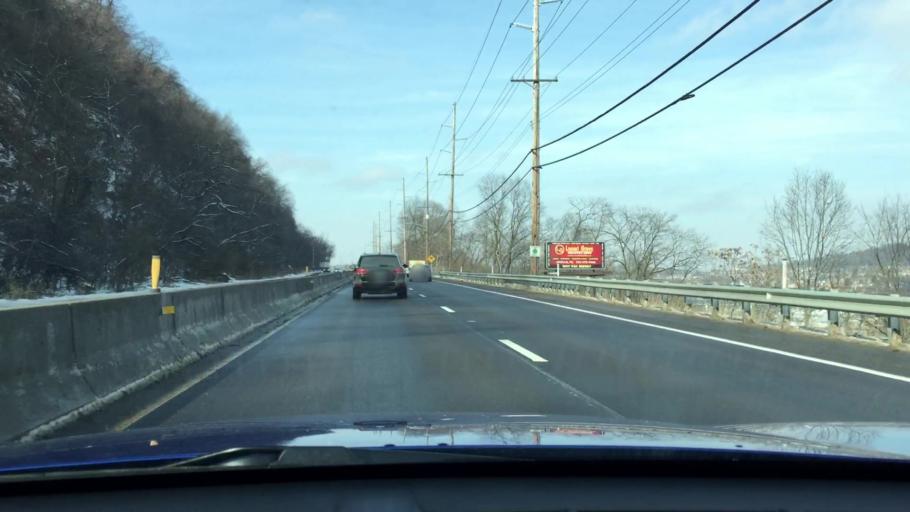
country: US
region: Pennsylvania
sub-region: Allegheny County
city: Braddock
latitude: 40.3950
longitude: -79.8725
